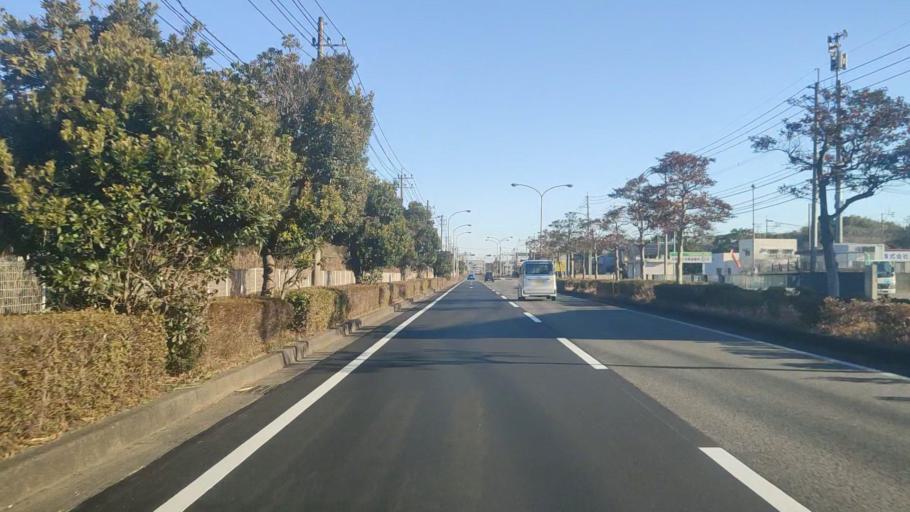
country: JP
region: Miyazaki
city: Nobeoka
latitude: 32.4525
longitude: 131.6413
